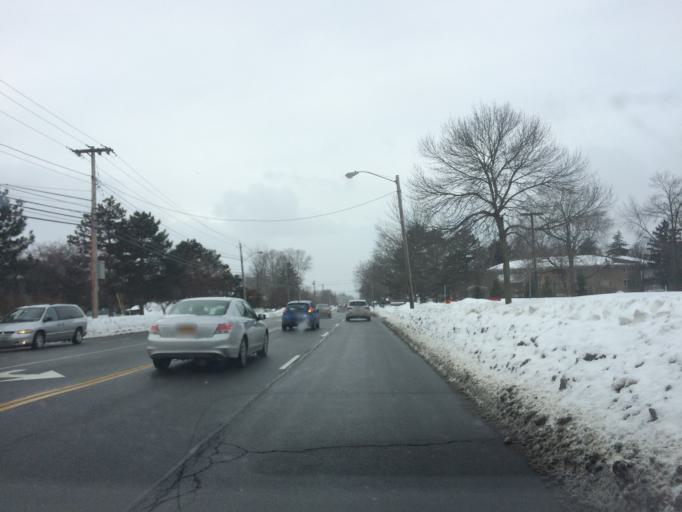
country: US
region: New York
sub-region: Monroe County
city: Rochester
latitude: 43.1257
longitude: -77.5933
